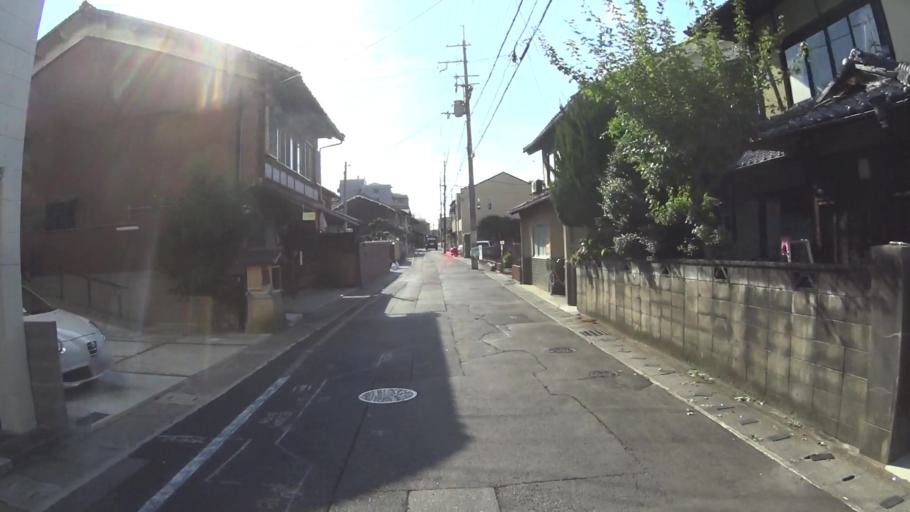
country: JP
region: Kyoto
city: Uji
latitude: 34.8871
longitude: 135.8052
